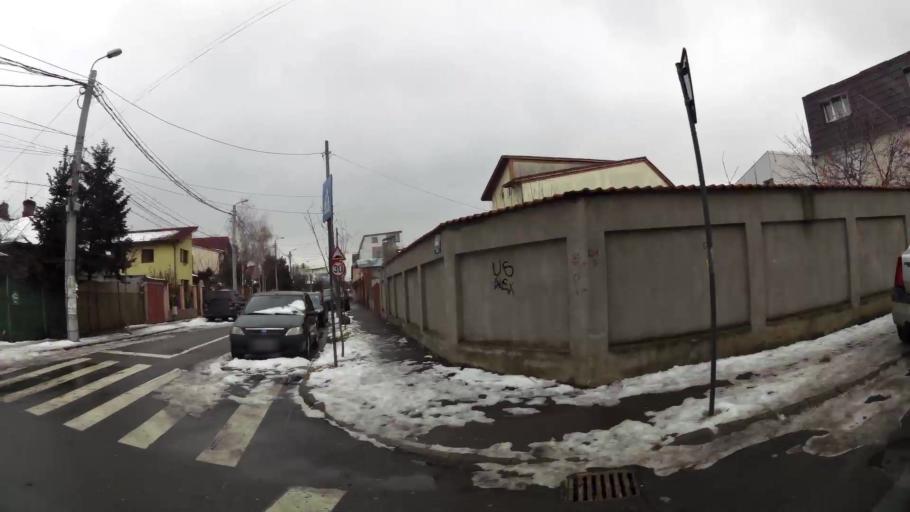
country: RO
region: Ilfov
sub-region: Comuna Chiajna
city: Rosu
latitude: 44.4861
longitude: 26.0319
